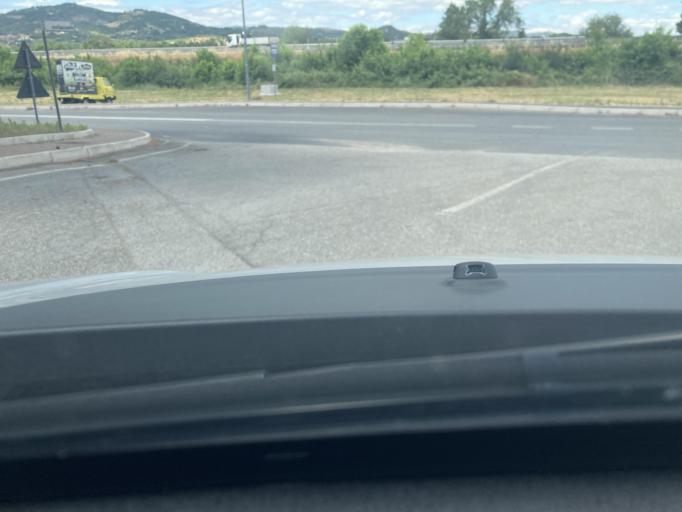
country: IT
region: Umbria
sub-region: Provincia di Perugia
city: Corciano
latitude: 43.1316
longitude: 12.2638
